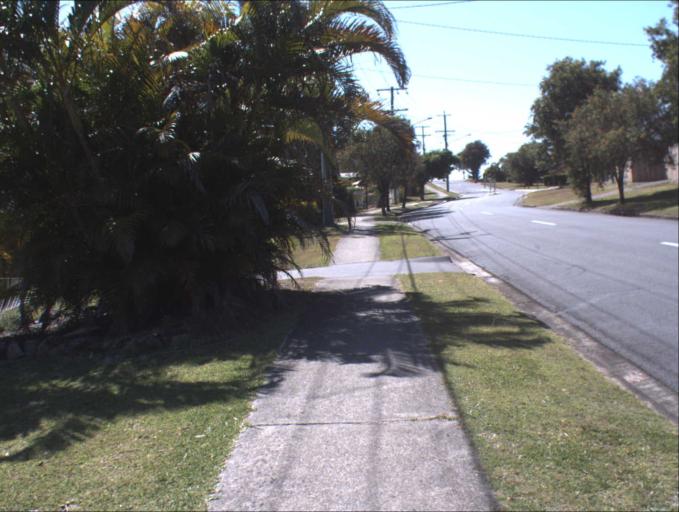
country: AU
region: Queensland
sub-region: Logan
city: Rochedale South
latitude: -27.6031
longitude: 153.1213
